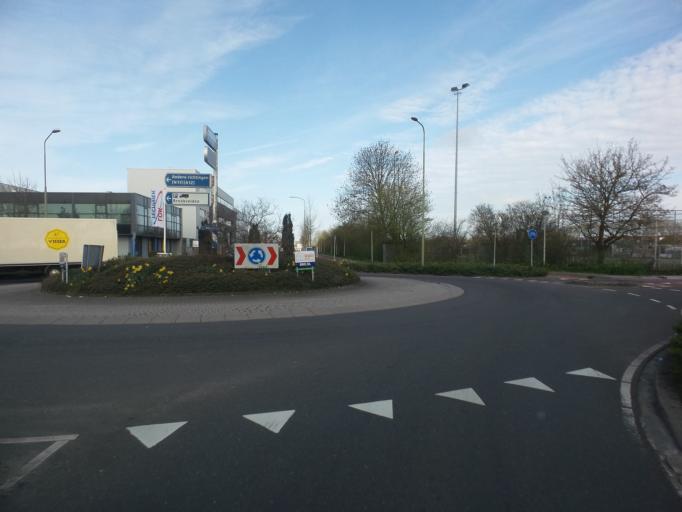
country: NL
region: South Holland
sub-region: Bodegraven-Reeuwijk
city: Bodegraven
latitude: 52.0722
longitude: 4.7483
